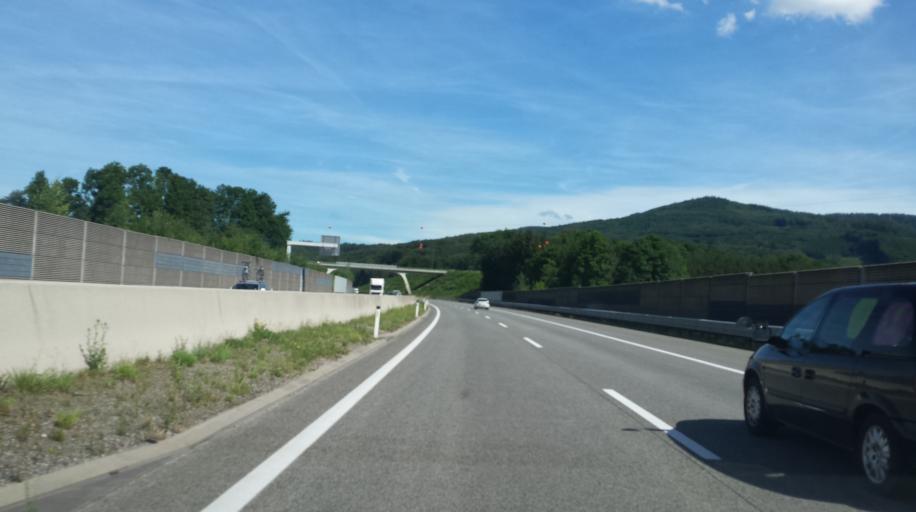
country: AT
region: Upper Austria
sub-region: Politischer Bezirk Vocklabruck
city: Aurach am Hongar
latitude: 47.9494
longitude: 13.6702
